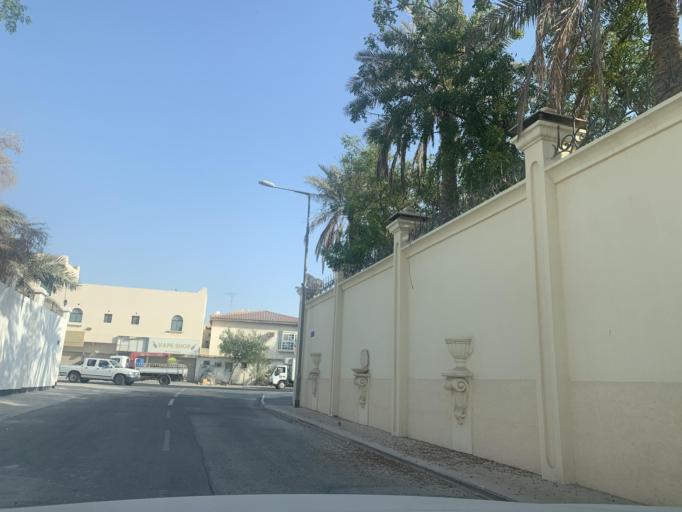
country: BH
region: Manama
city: Jidd Hafs
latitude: 26.1968
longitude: 50.4845
